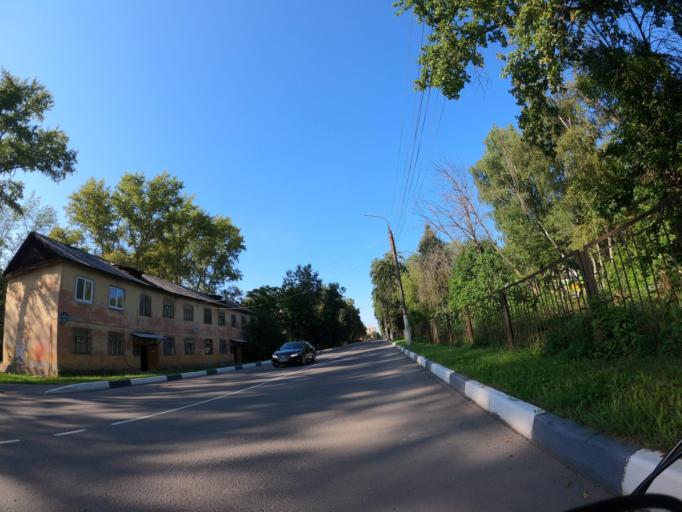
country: RU
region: Moskovskaya
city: Stupino
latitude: 54.8822
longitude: 38.0712
